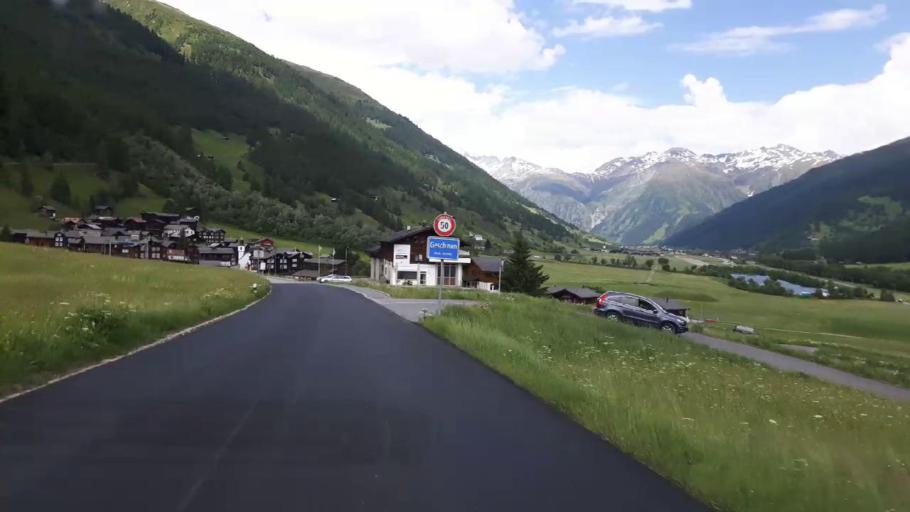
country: CH
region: Valais
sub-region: Goms District
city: Fiesch
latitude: 46.4922
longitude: 8.2784
